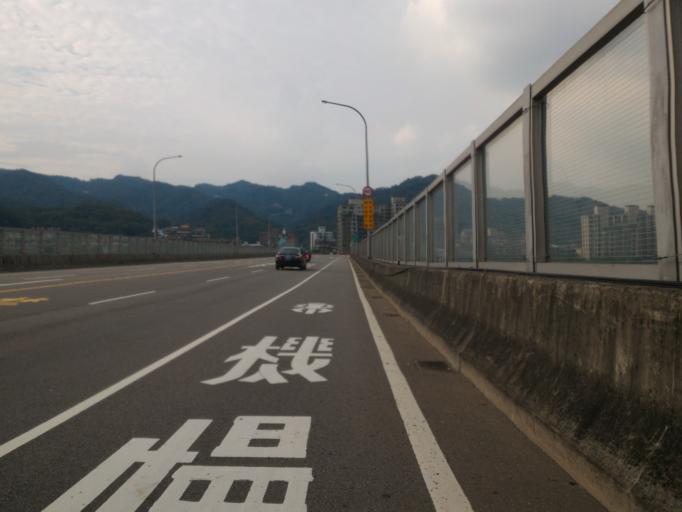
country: TW
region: Taiwan
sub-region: Taoyuan
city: Taoyuan
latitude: 24.9652
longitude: 121.3946
